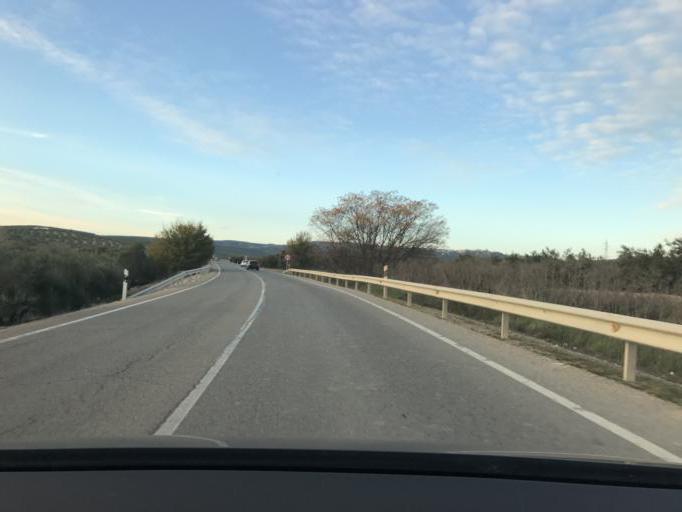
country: ES
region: Andalusia
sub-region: Provincia de Jaen
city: Ubeda
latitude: 37.9617
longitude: -3.3592
